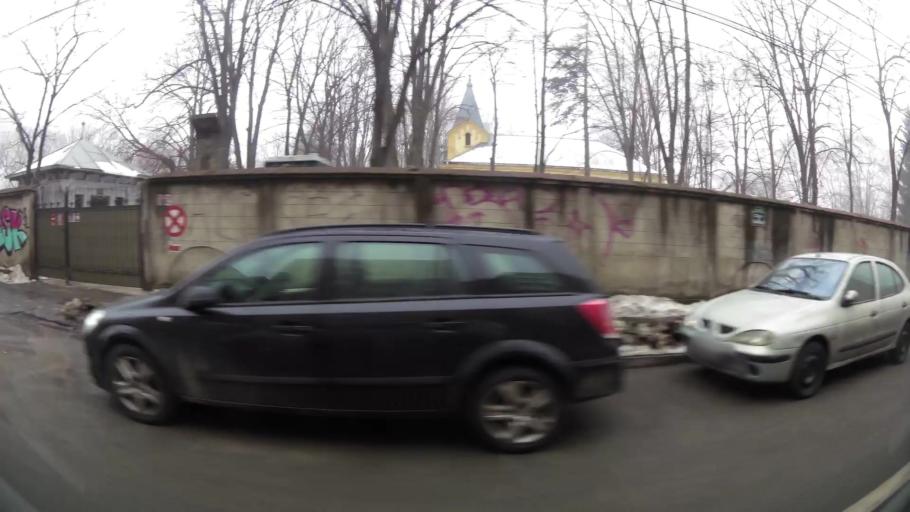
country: RO
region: Ilfov
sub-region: Comuna Chiajna
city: Rosu
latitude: 44.4573
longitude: 26.0540
